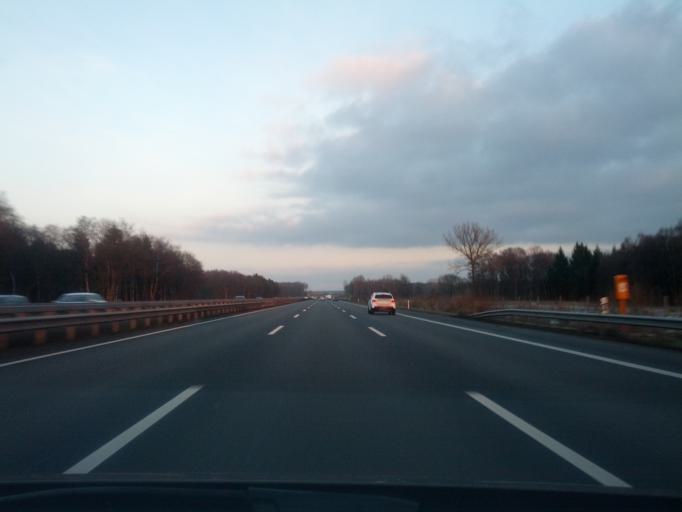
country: DE
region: Lower Saxony
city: Halvesbostel
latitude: 53.3203
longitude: 9.5817
